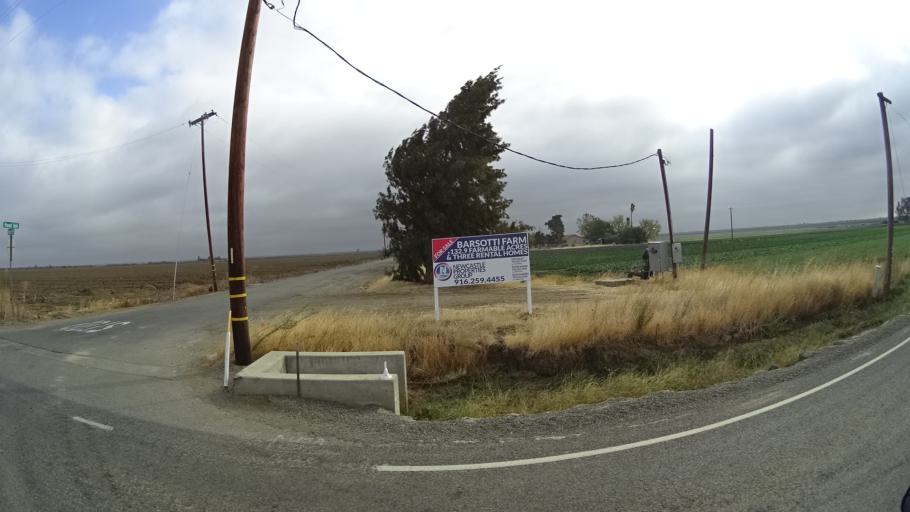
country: US
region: California
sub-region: Yolo County
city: Esparto
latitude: 38.7450
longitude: -122.0448
